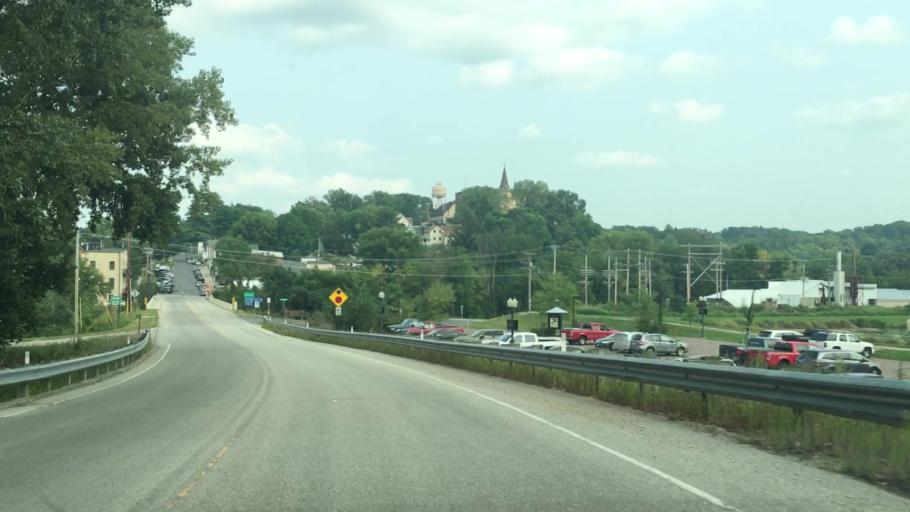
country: US
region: Minnesota
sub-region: Fillmore County
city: Preston
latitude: 43.7209
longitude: -91.9798
